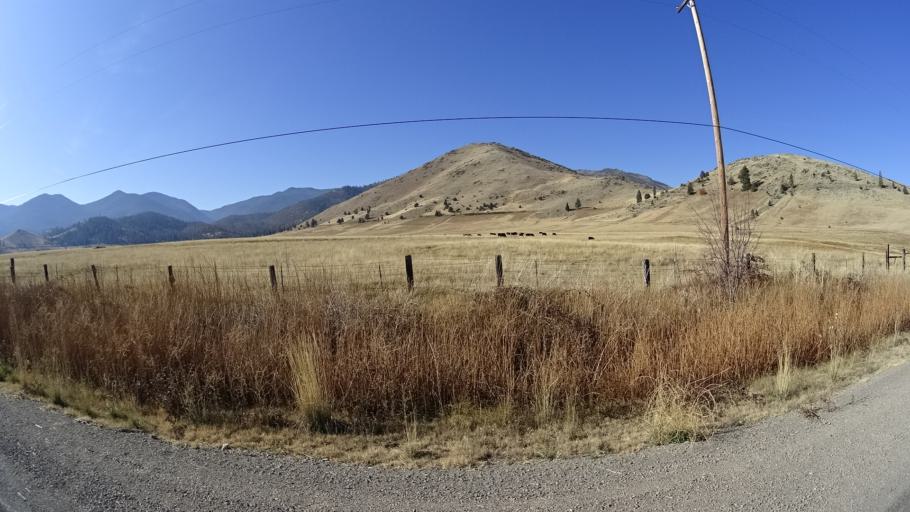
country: US
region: California
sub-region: Siskiyou County
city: Weed
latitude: 41.4628
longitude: -122.4642
